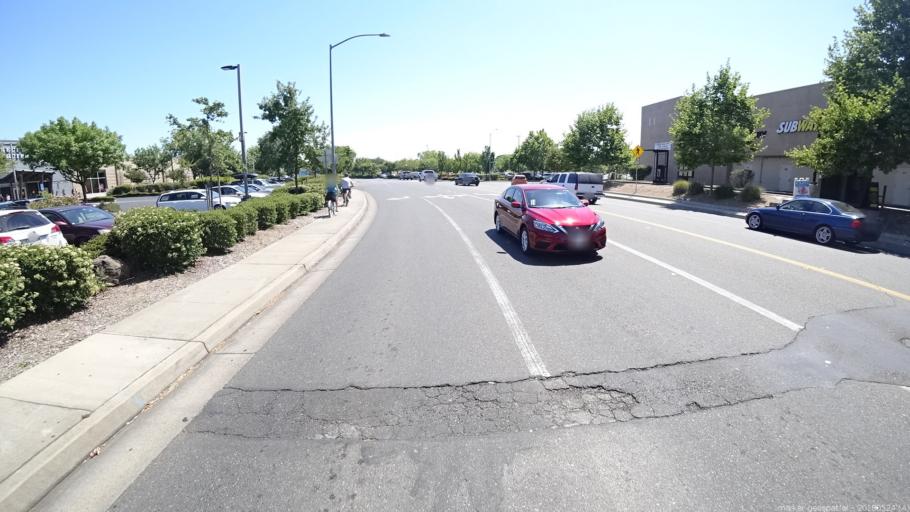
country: US
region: California
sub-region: Sacramento County
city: Sacramento
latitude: 38.5983
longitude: -121.4504
